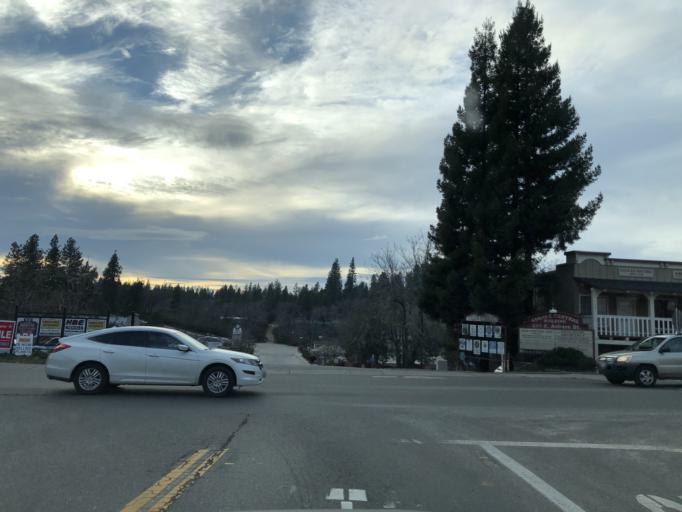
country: US
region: California
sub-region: Placer County
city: Colfax
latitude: 39.0969
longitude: -120.9507
